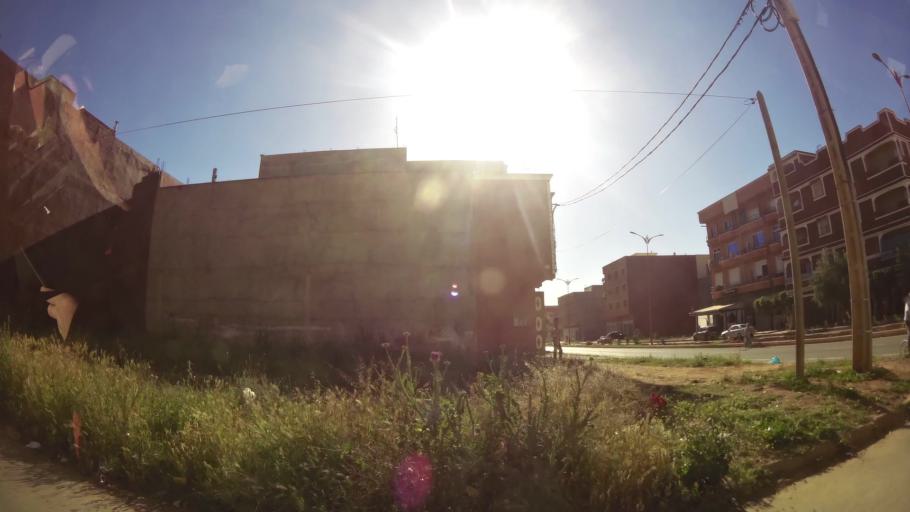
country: MA
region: Oriental
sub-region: Berkane-Taourirt
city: Berkane
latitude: 34.9341
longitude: -2.3327
